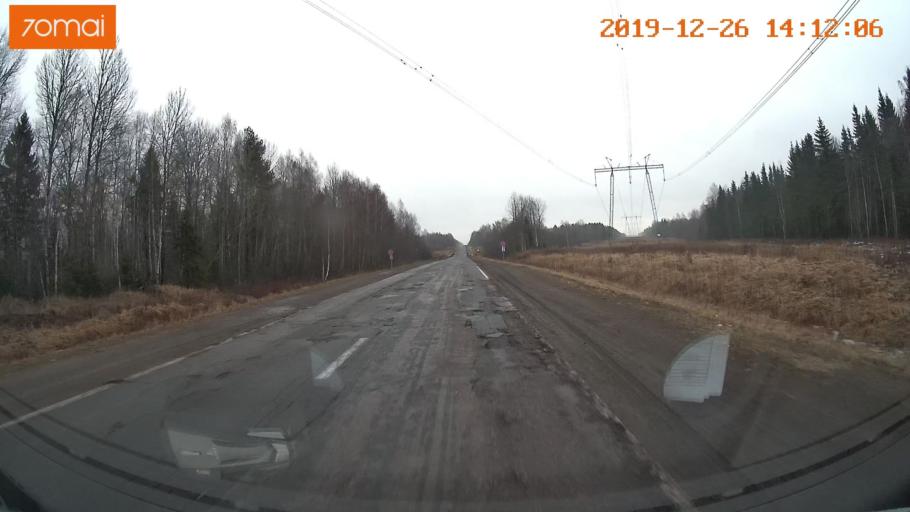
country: RU
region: Jaroslavl
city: Poshekhon'ye
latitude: 58.5106
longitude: 38.9849
